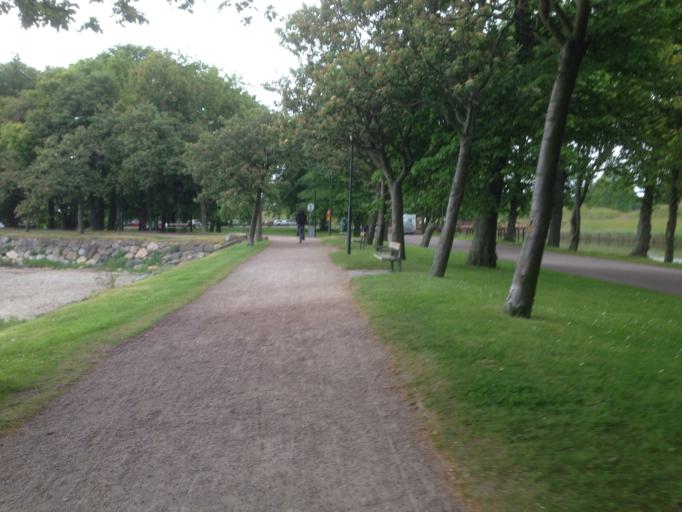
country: SE
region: Skane
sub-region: Landskrona
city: Landskrona
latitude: 55.8710
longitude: 12.8212
